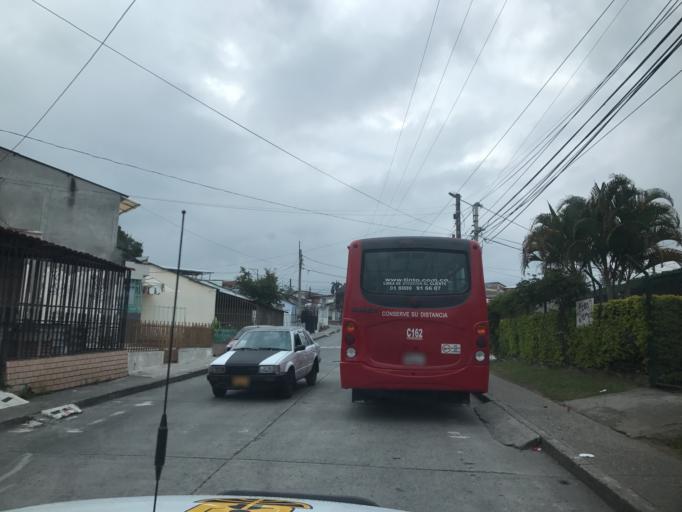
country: CO
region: Quindio
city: Armenia
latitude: 4.5352
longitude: -75.6934
